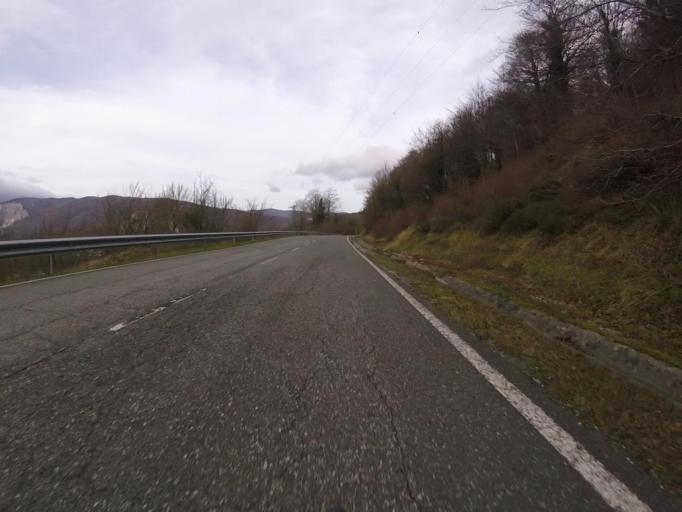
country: ES
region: Navarre
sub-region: Provincia de Navarra
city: Olazagutia
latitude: 42.8624
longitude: -2.1855
